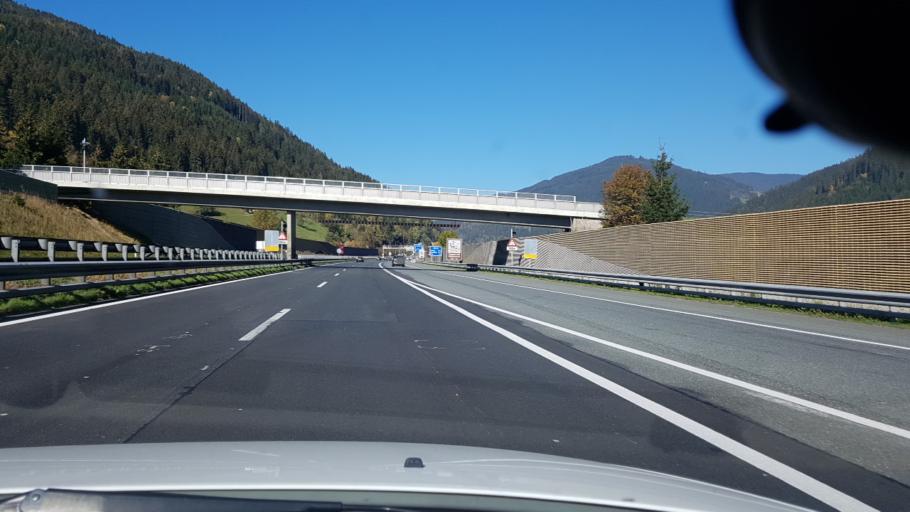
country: AT
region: Salzburg
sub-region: Politischer Bezirk Sankt Johann im Pongau
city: Eben im Pongau
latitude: 47.3948
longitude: 13.3968
